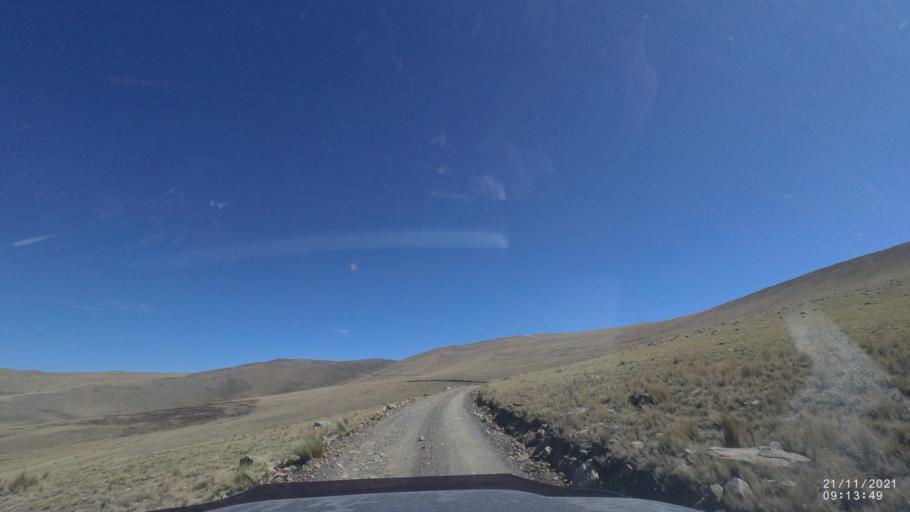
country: BO
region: Cochabamba
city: Cochabamba
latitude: -17.1383
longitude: -66.2577
